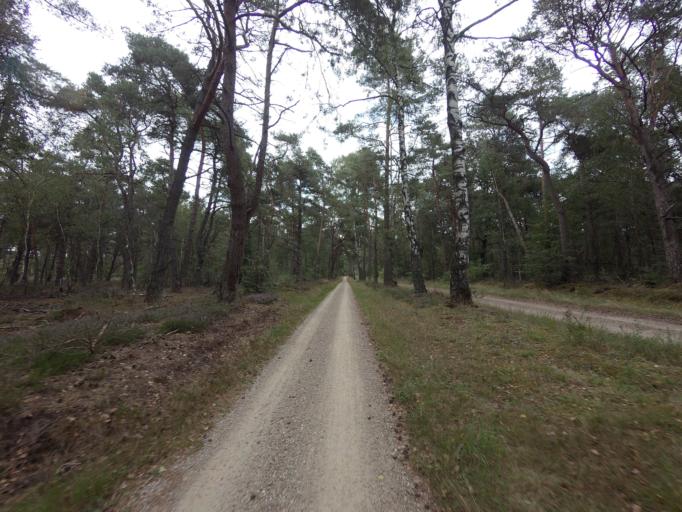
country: NL
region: Overijssel
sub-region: Gemeente Hof van Twente
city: Markelo
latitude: 52.2969
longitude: 6.4519
